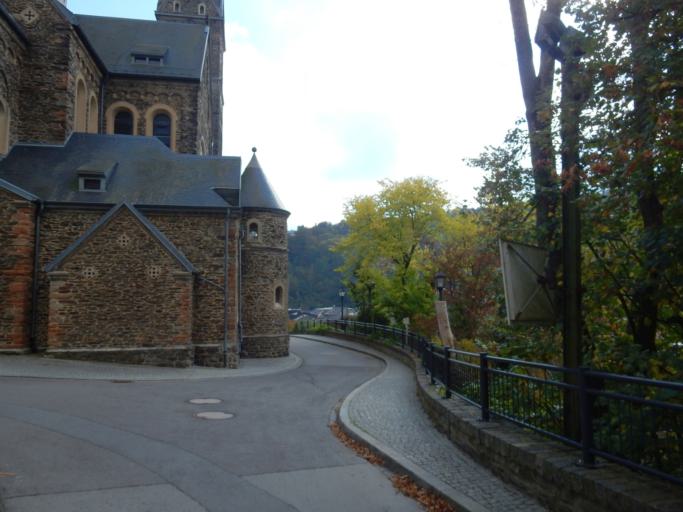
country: LU
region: Diekirch
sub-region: Canton de Clervaux
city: Clervaux
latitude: 50.0555
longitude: 6.0279
